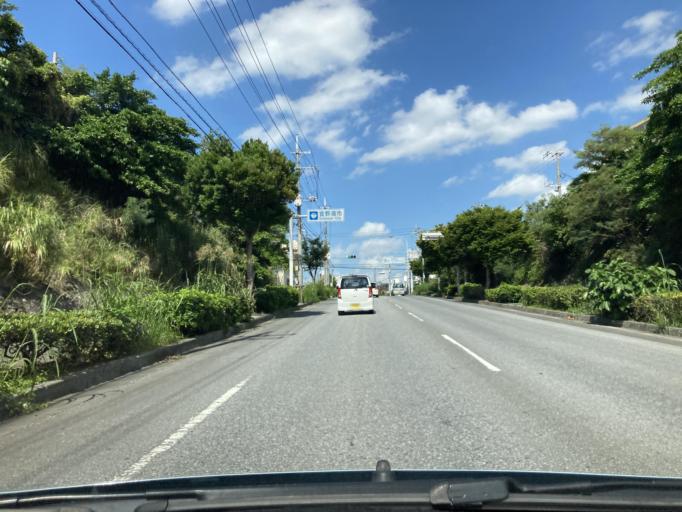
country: JP
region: Okinawa
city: Ginowan
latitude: 26.2497
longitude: 127.7575
